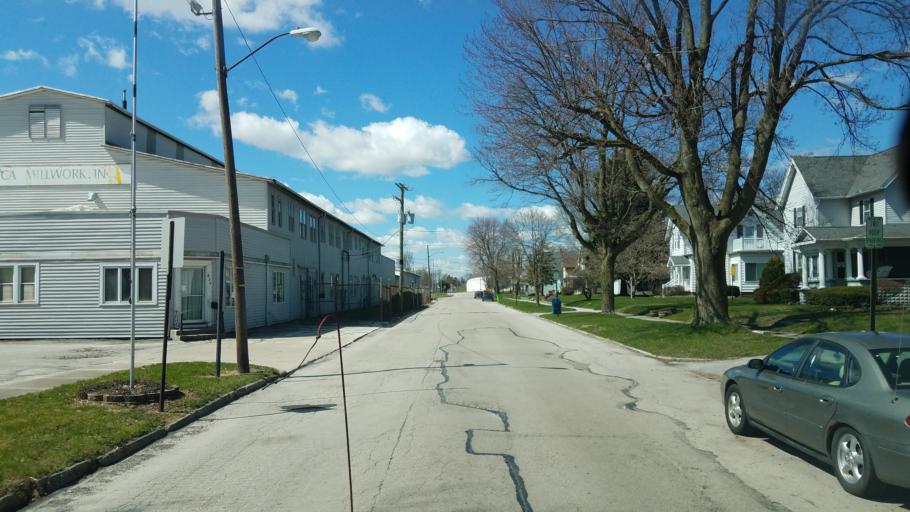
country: US
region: Ohio
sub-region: Seneca County
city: Fostoria
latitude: 41.1563
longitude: -83.4266
